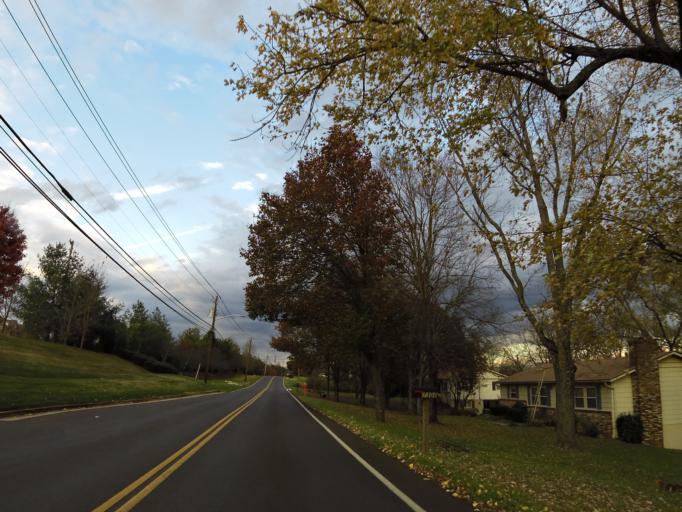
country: US
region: Tennessee
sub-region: Blount County
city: Louisville
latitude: 35.9208
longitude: -84.0266
